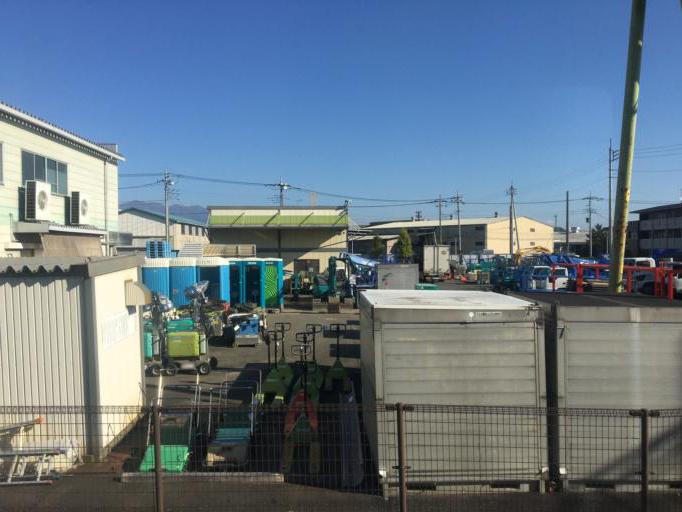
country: JP
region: Gunma
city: Maebashi-shi
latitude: 36.3702
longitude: 139.1104
